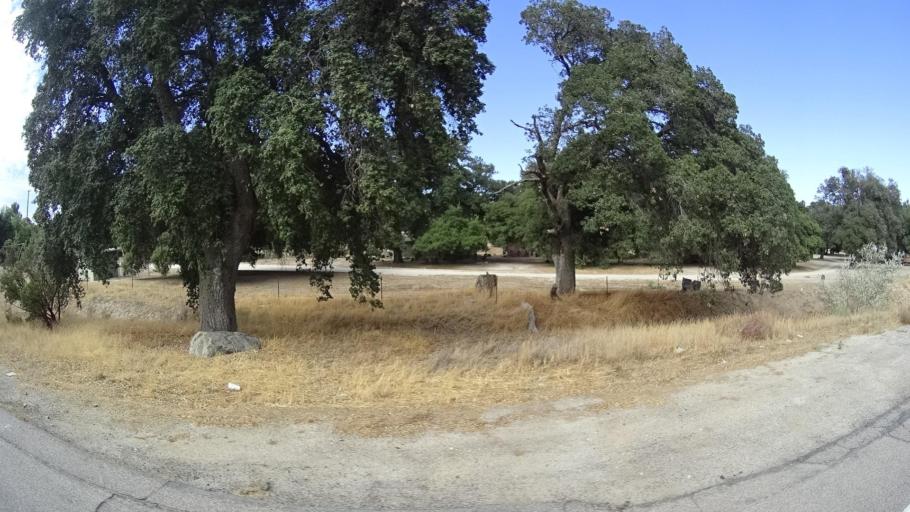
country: MX
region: Baja California
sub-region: Tecate
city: Cereso del Hongo
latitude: 32.6656
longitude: -116.2802
